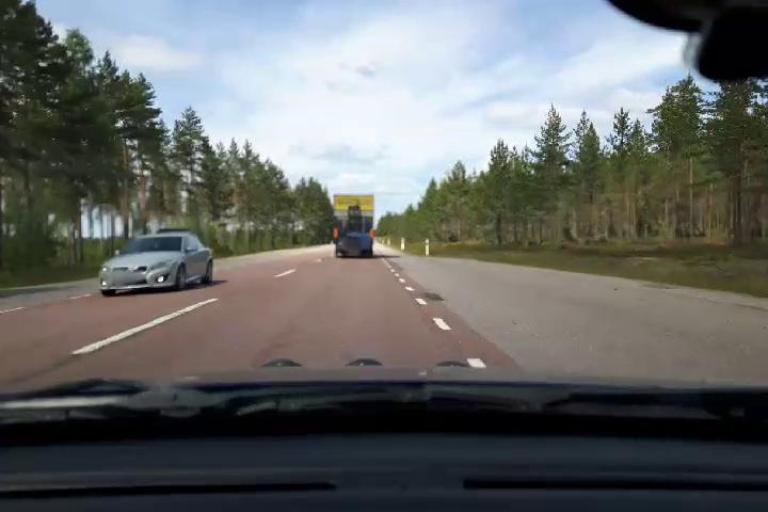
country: SE
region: Uppsala
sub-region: Osthammars Kommun
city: Bjorklinge
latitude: 60.1751
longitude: 17.4849
